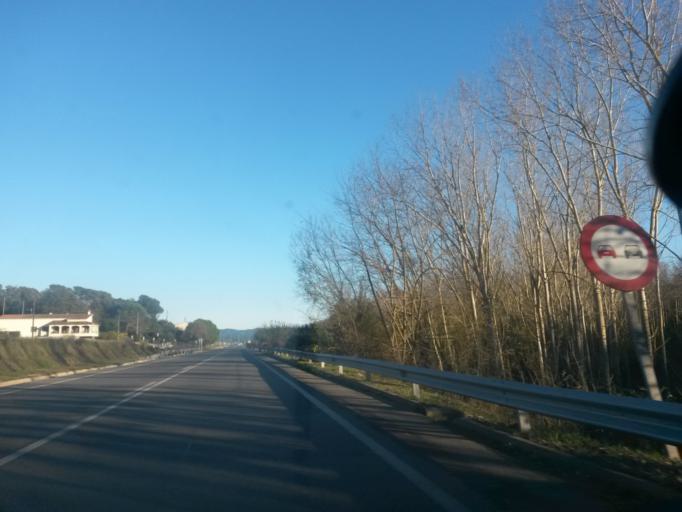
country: ES
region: Catalonia
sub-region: Provincia de Girona
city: Aiguaviva
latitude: 41.9383
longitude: 2.7727
